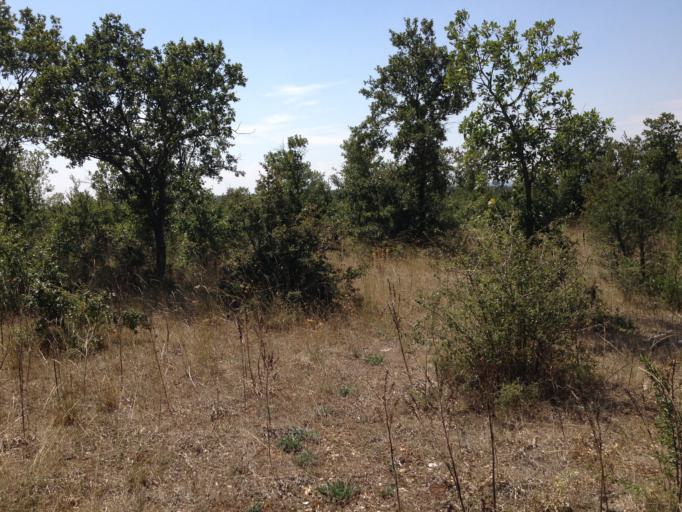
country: IT
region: Apulia
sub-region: Provincia di Bari
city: Gioia del Colle
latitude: 40.8270
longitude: 16.9901
